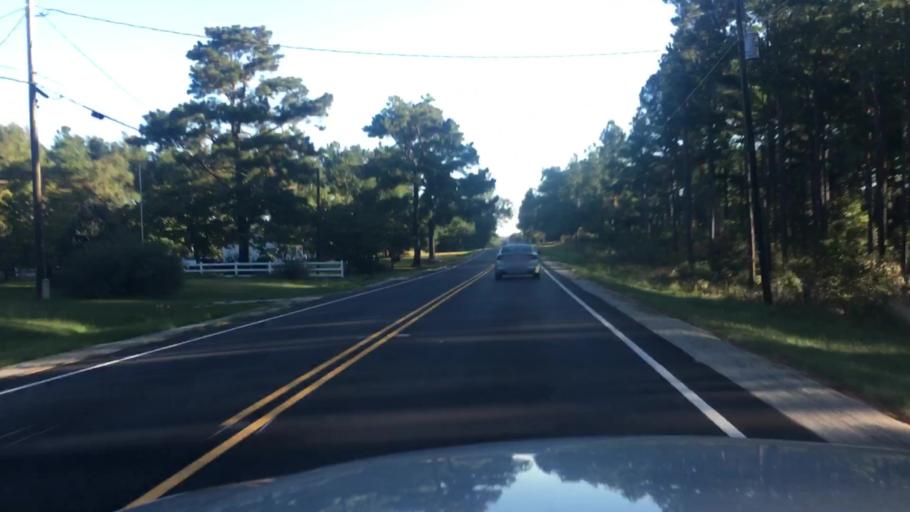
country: US
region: North Carolina
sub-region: Harnett County
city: Walkertown
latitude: 35.3332
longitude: -78.8614
